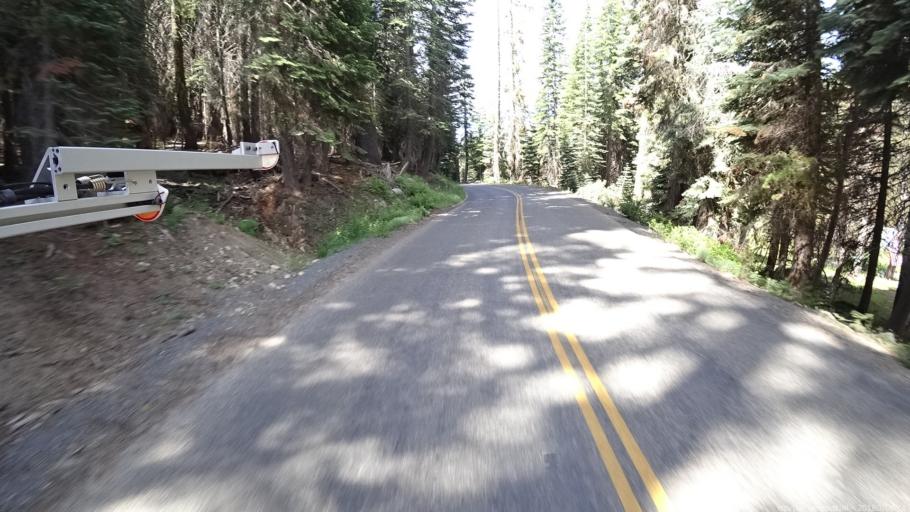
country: US
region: California
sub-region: Madera County
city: Oakhurst
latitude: 37.4394
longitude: -119.4773
